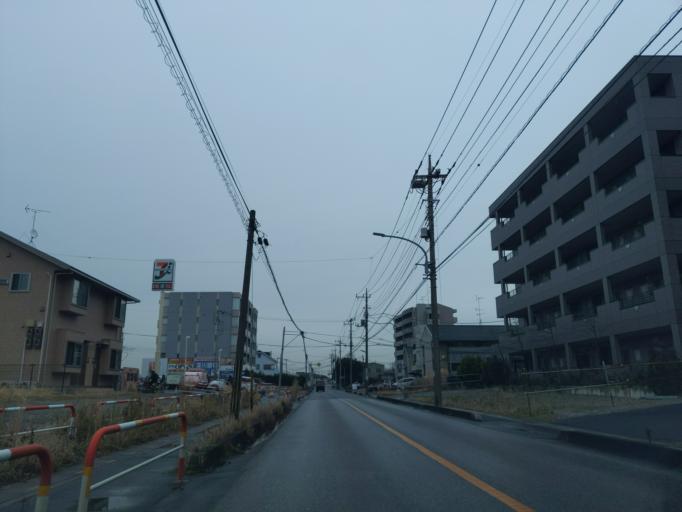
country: JP
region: Saitama
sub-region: Kawaguchi-shi
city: Hatogaya-honcho
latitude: 35.8587
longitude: 139.7492
